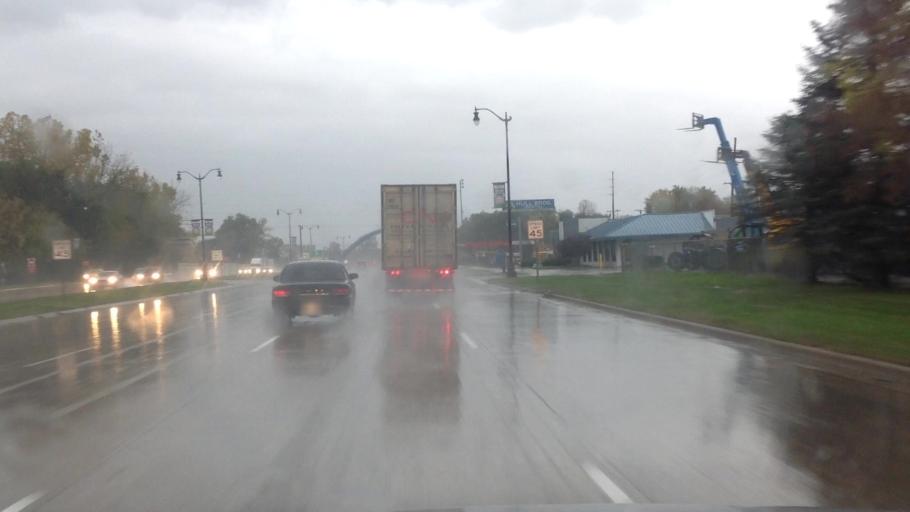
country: US
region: Michigan
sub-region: Wayne County
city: Taylor
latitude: 42.2579
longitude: -83.2701
